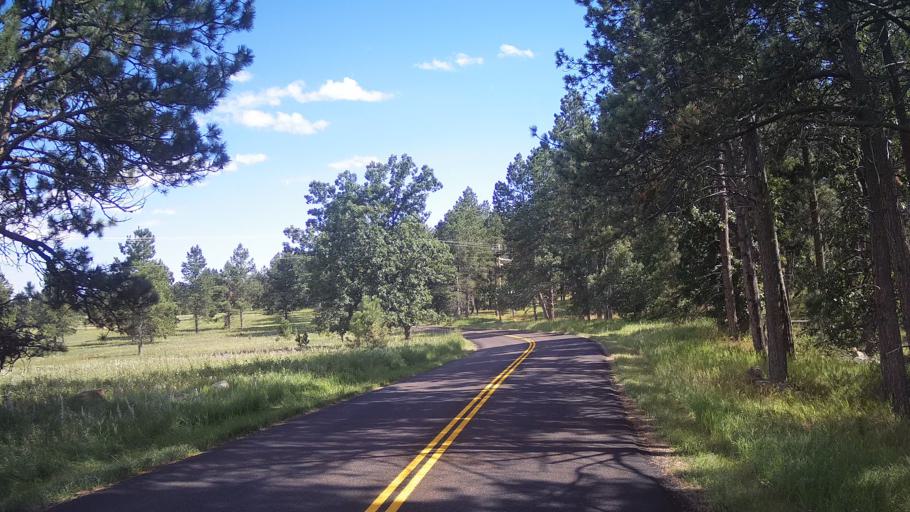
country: US
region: South Dakota
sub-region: Pennington County
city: Colonial Pine Hills
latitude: 43.8436
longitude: -103.3999
